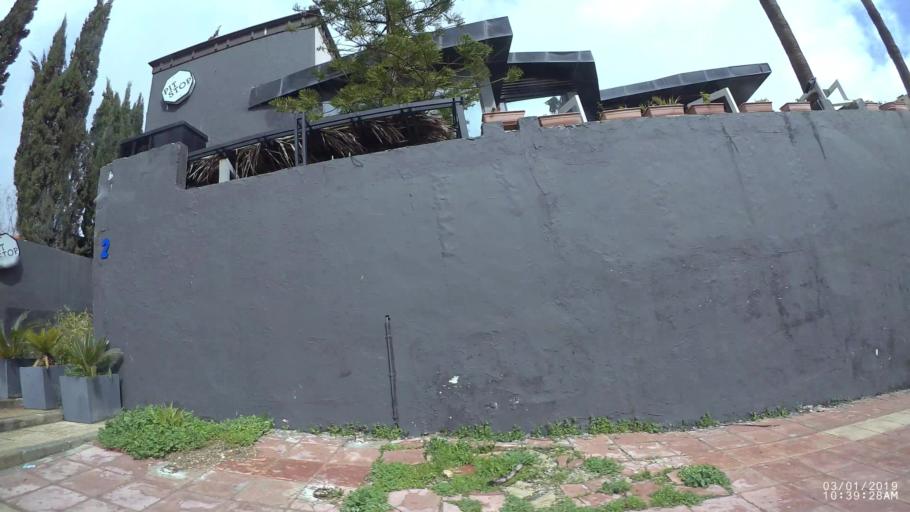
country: JO
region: Amman
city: Wadi as Sir
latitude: 31.9510
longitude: 35.8520
